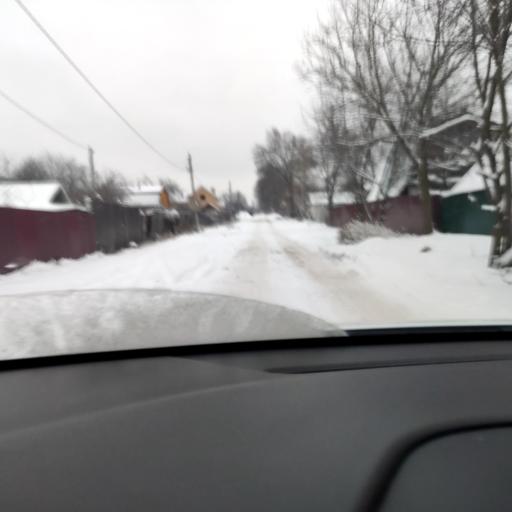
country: RU
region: Tatarstan
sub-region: Gorod Kazan'
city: Kazan
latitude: 55.8386
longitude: 49.2147
